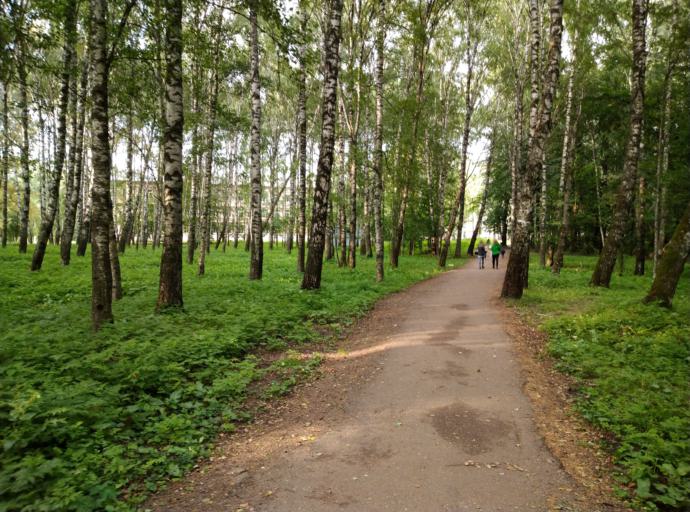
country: RU
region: Kostroma
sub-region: Kostromskoy Rayon
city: Kostroma
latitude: 57.7619
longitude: 40.9643
